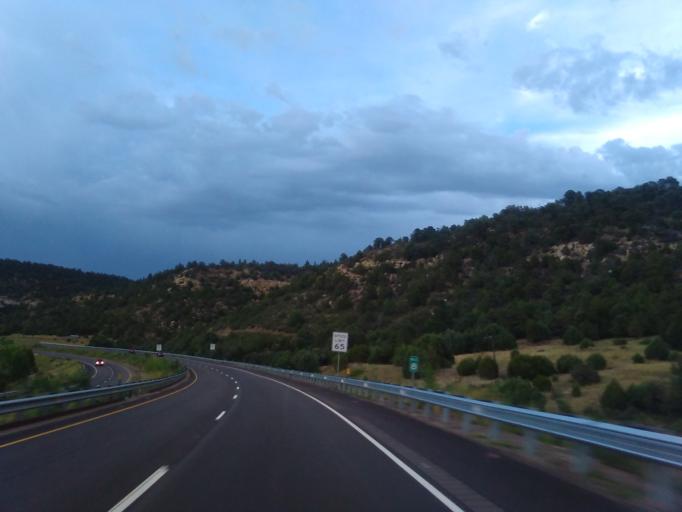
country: US
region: Colorado
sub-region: Las Animas County
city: Trinidad
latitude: 37.0914
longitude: -104.5199
